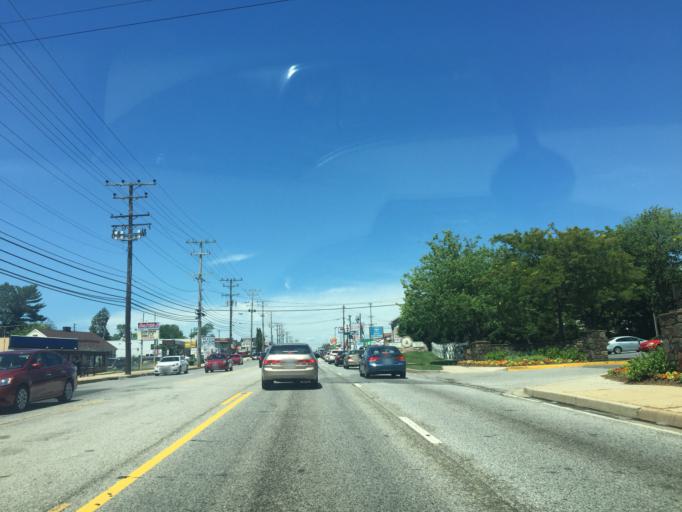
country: US
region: Maryland
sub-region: Baltimore County
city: Milford Mill
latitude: 39.3521
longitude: -76.7535
